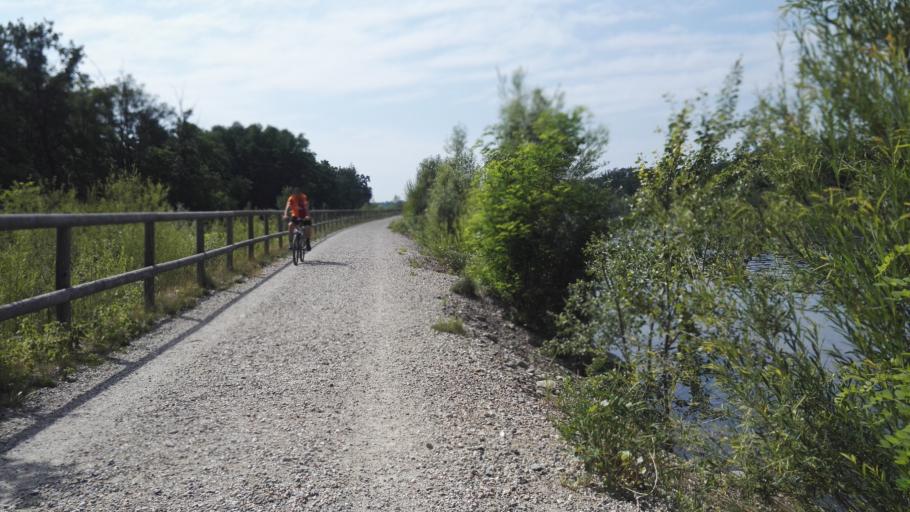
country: AT
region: Styria
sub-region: Politischer Bezirk Graz-Umgebung
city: Feldkirchen bei Graz
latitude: 47.0071
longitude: 15.4637
